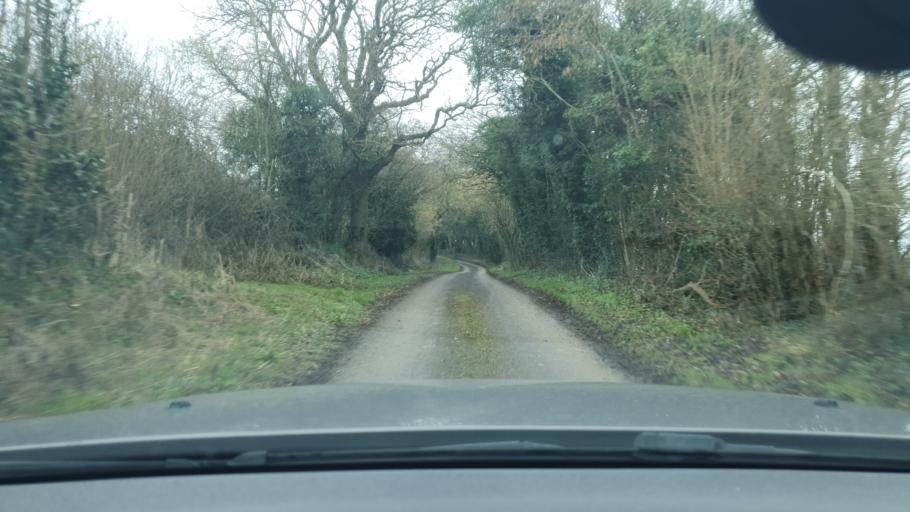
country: GB
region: England
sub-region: Wiltshire
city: Ramsbury
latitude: 51.4657
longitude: -1.5935
